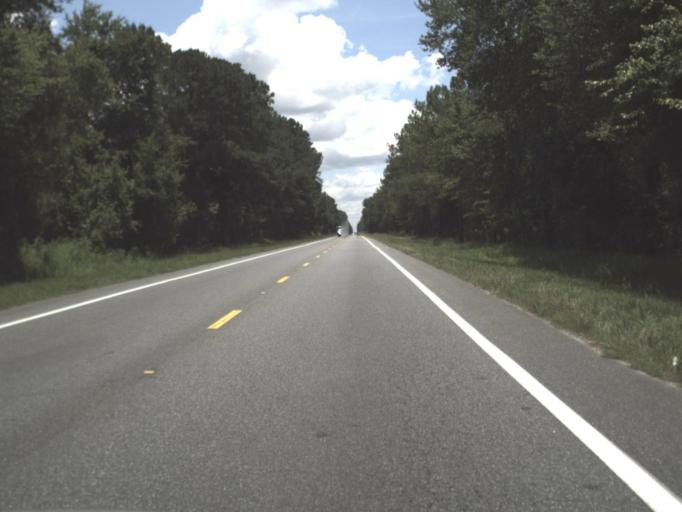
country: US
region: Florida
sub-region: Columbia County
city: Five Points
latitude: 30.2392
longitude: -82.6705
